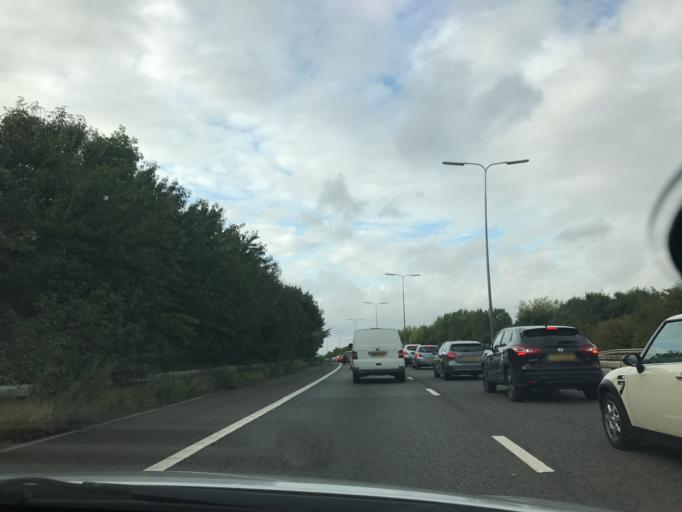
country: GB
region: England
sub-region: Cheshire West and Chester
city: Ellesmere Port
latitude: 53.2801
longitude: -2.8853
